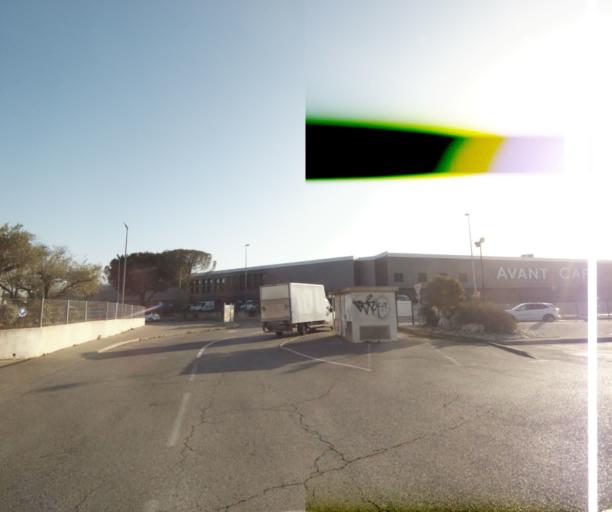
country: FR
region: Provence-Alpes-Cote d'Azur
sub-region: Departement des Bouches-du-Rhone
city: Septemes-les-Vallons
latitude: 43.4192
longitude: 5.3590
